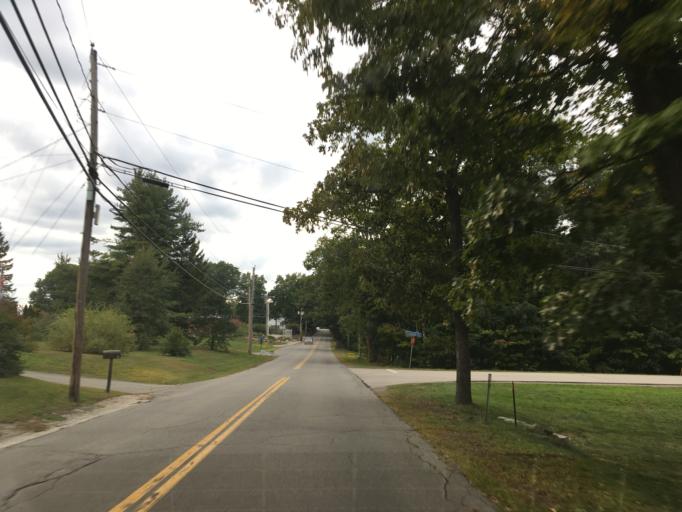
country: US
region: New Hampshire
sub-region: Rockingham County
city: Exeter
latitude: 43.0109
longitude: -70.9134
